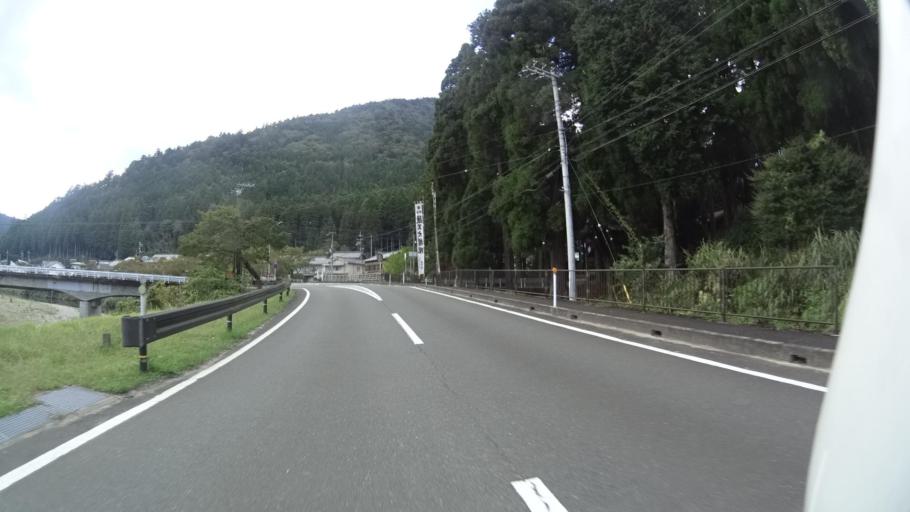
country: JP
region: Fukui
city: Obama
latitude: 35.3134
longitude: 135.6423
